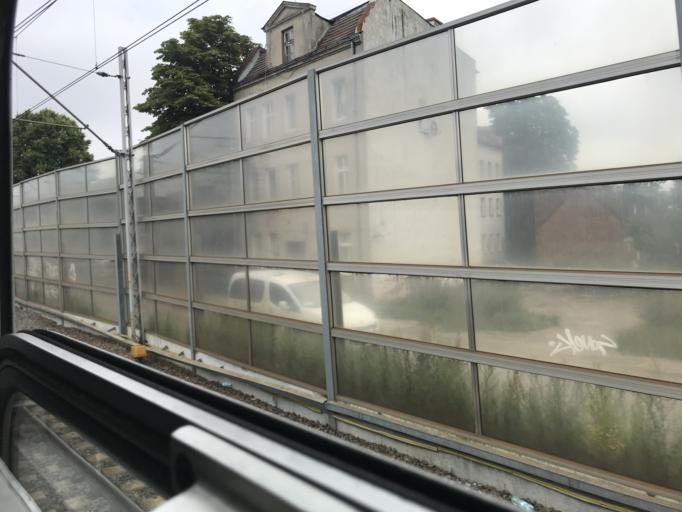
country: PL
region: Pomeranian Voivodeship
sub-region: Gdansk
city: Gdansk
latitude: 54.3306
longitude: 18.6364
